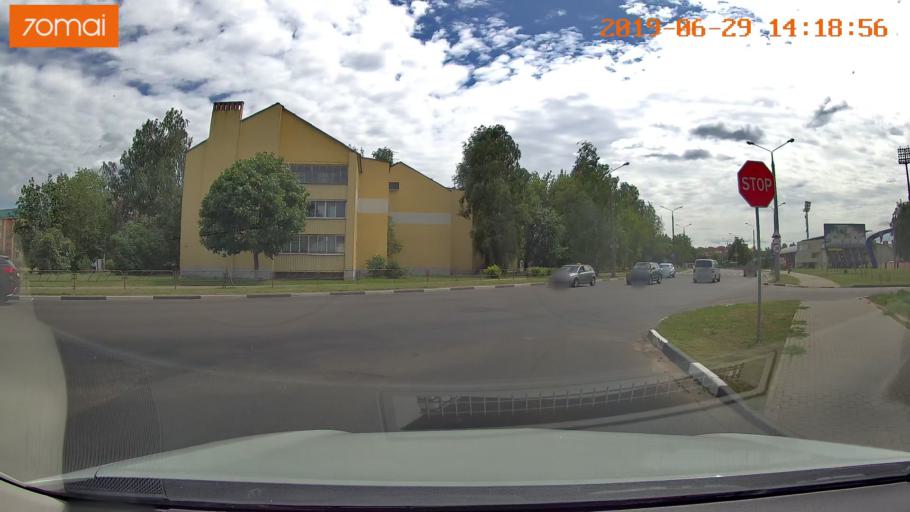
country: BY
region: Minsk
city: Salihorsk
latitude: 52.8007
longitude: 27.5403
